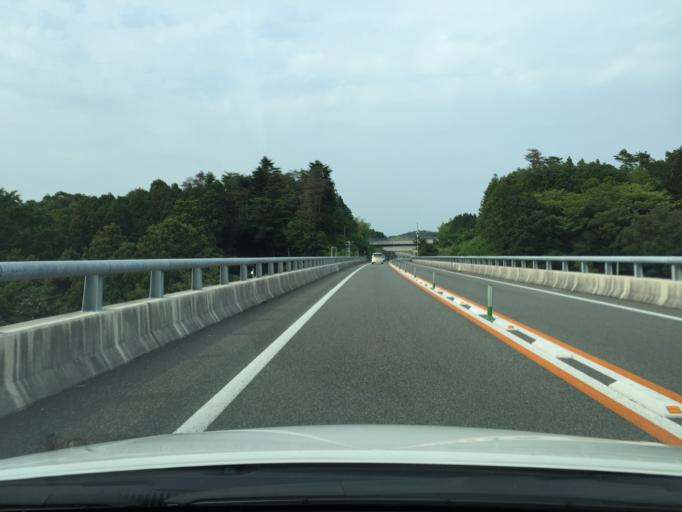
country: JP
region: Fukushima
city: Namie
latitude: 37.2953
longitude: 140.9849
